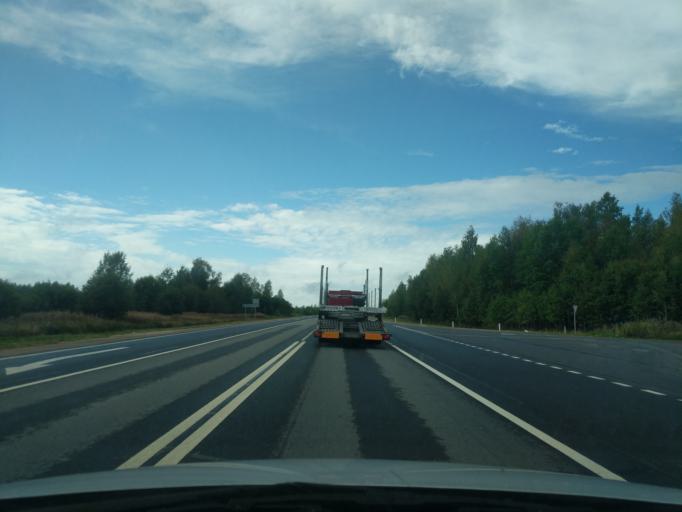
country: RU
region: Kostroma
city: Sudislavl'
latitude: 57.8176
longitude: 41.9450
